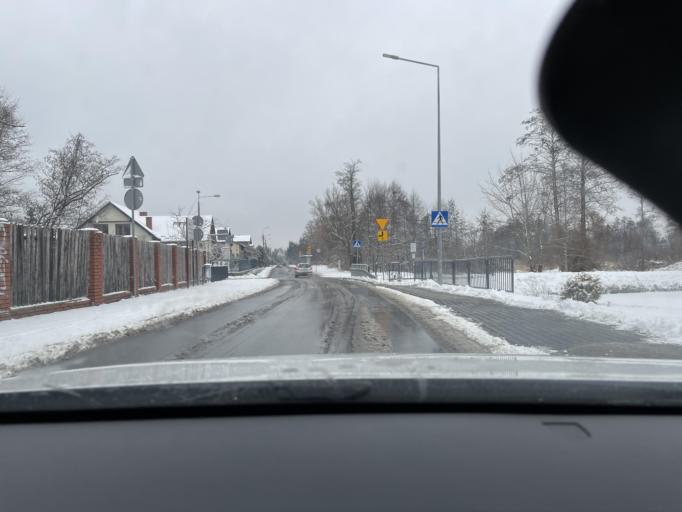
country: PL
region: Masovian Voivodeship
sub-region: Powiat zyrardowski
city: Zyrardow
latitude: 52.0425
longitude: 20.4462
